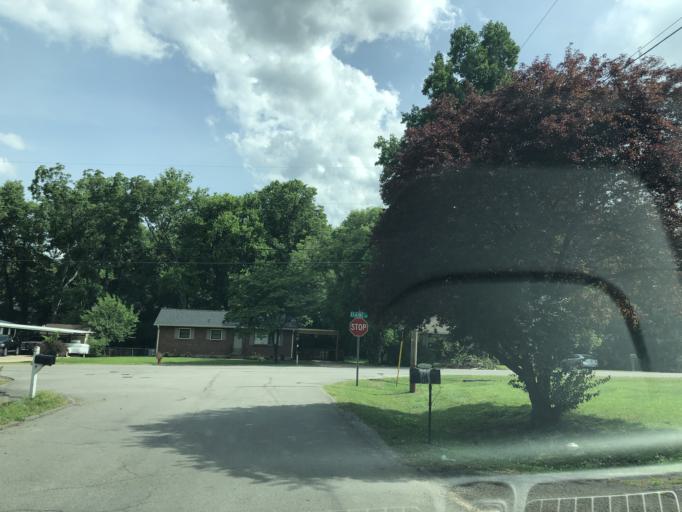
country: US
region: Tennessee
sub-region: Davidson County
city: Oak Hill
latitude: 36.0827
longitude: -86.7477
